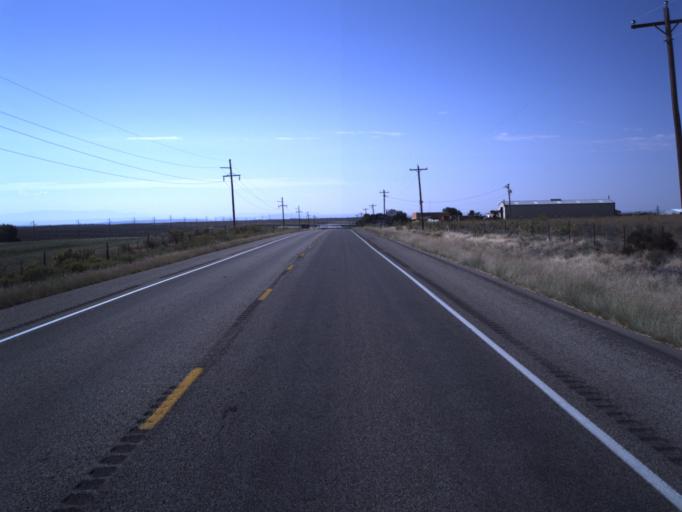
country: US
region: Utah
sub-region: San Juan County
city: Blanding
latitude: 37.5863
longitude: -109.4783
